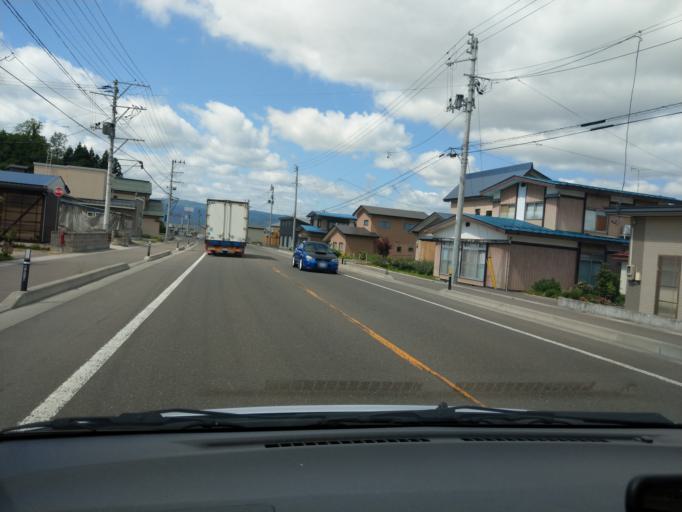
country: JP
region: Akita
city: Yuzawa
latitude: 39.1798
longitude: 140.4946
